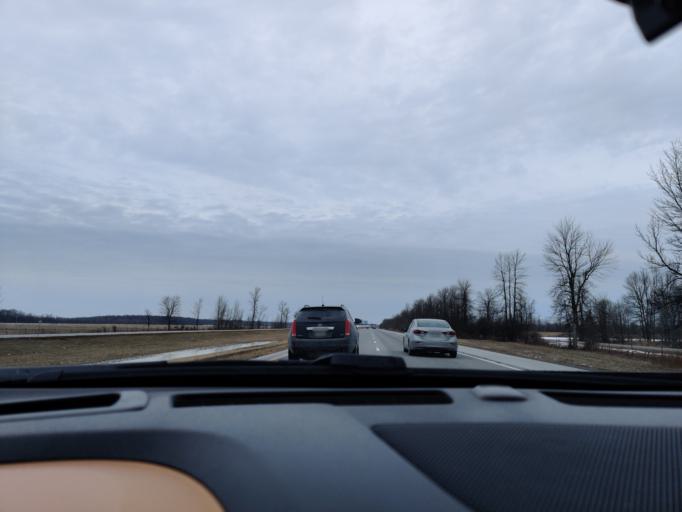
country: US
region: New York
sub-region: St. Lawrence County
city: Norfolk
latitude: 44.9021
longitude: -75.2339
